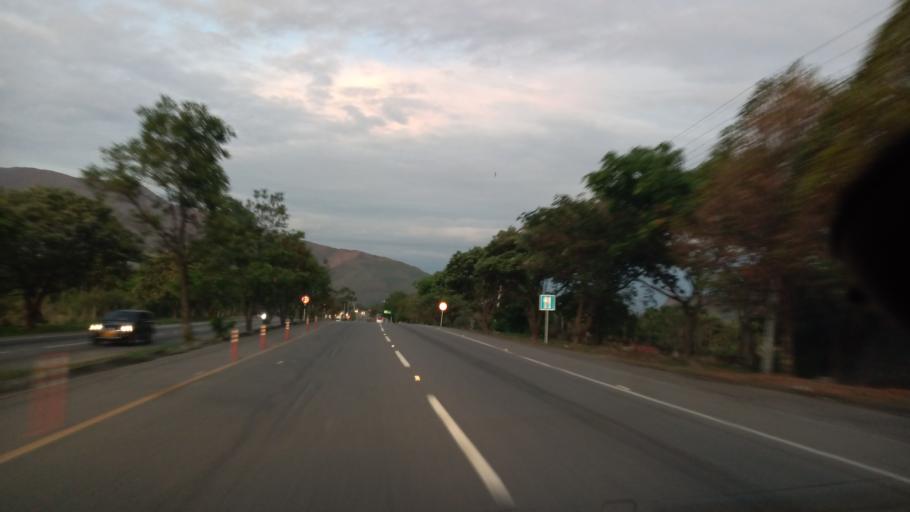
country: CO
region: Cundinamarca
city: Pandi
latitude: 4.2633
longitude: -74.5198
